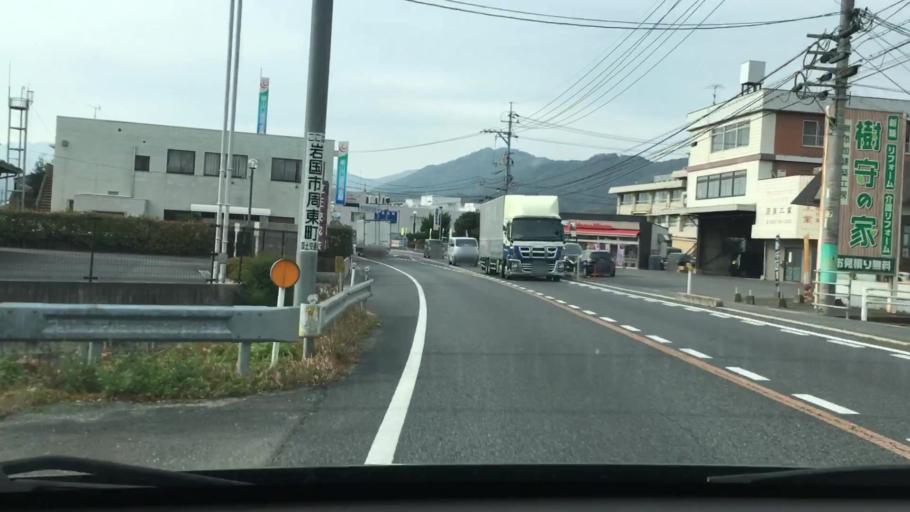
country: JP
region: Yamaguchi
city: Yanai
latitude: 34.0927
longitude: 132.0543
